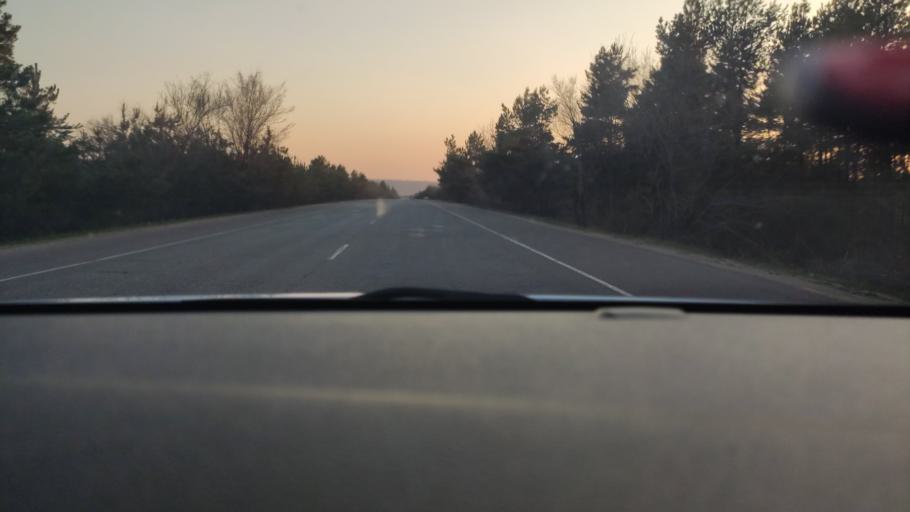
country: RU
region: Voronezj
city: Kolodeznyy
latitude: 51.3640
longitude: 39.1919
